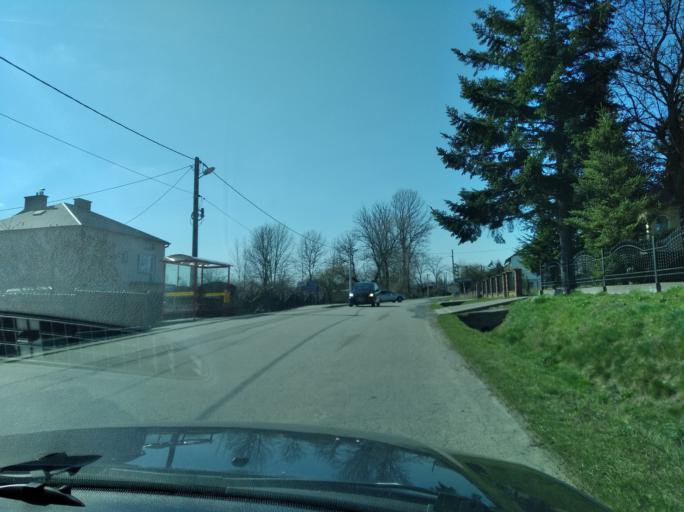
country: PL
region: Subcarpathian Voivodeship
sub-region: Powiat jaroslawski
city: Pruchnik
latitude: 49.9293
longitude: 22.4890
